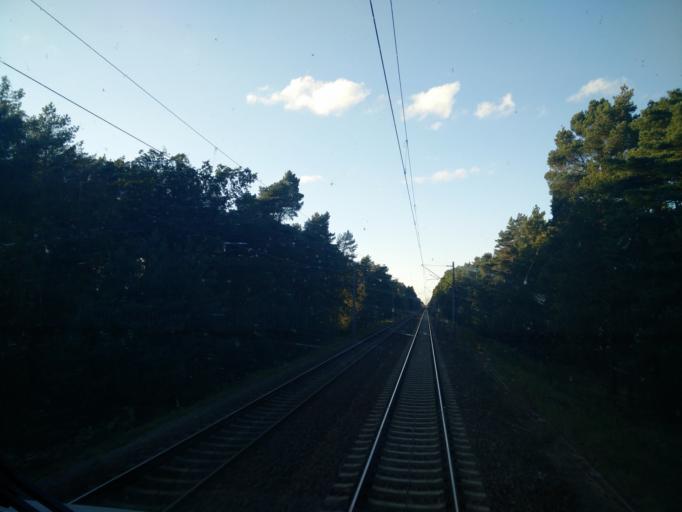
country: DE
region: Brandenburg
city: Dreetz
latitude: 52.8222
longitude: 12.4962
